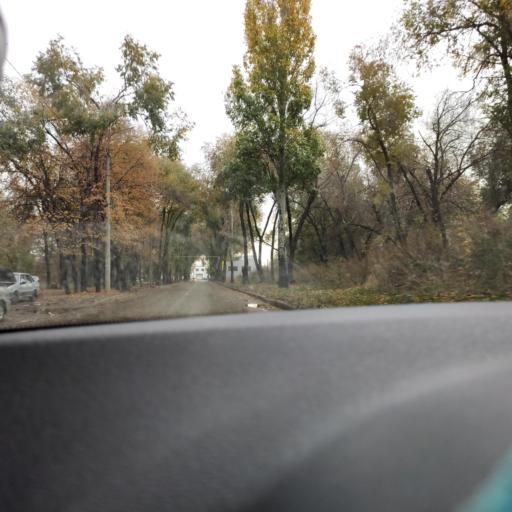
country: RU
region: Samara
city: Samara
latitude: 53.1999
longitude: 50.2443
